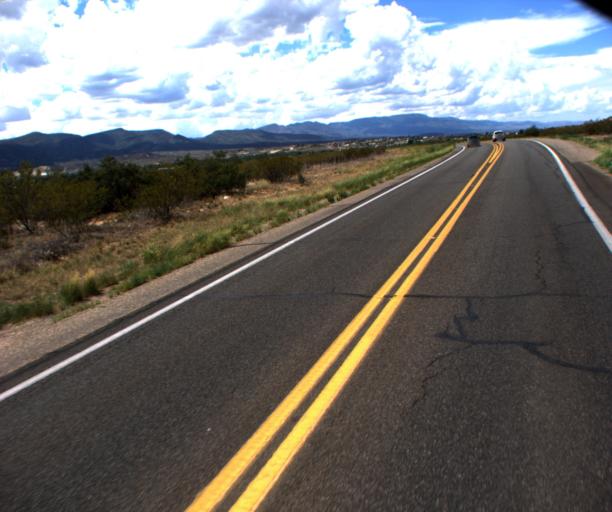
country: US
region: Arizona
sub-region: Yavapai County
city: Camp Verde
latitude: 34.5466
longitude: -111.8309
